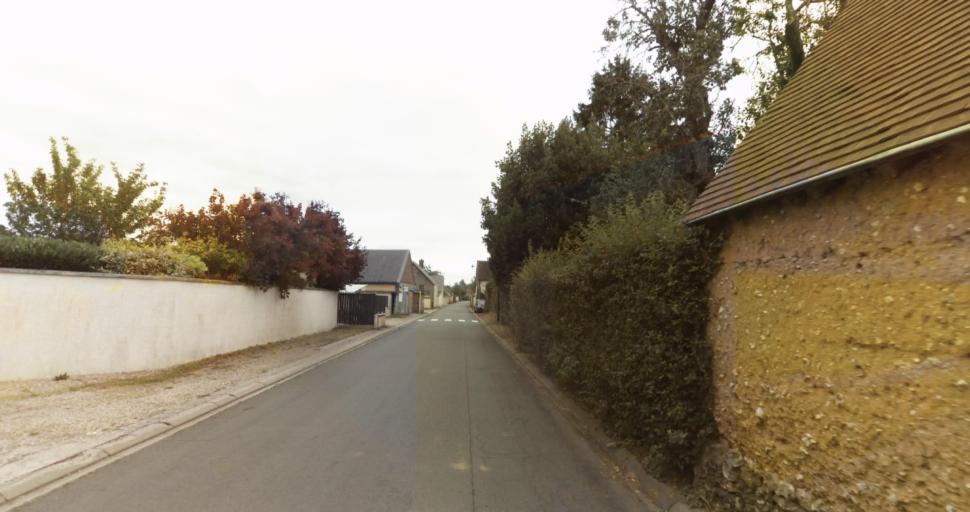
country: FR
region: Haute-Normandie
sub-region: Departement de l'Eure
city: Gravigny
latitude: 48.9894
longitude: 1.2479
